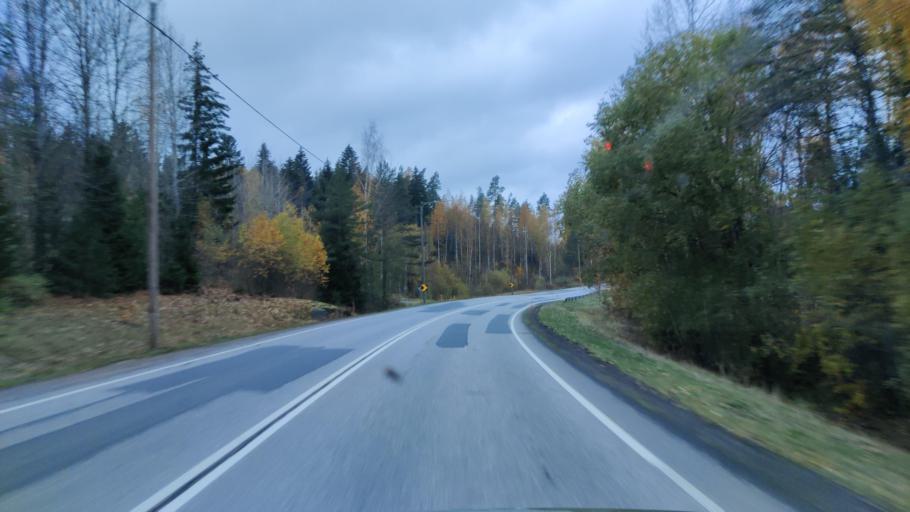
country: FI
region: Uusimaa
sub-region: Helsinki
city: Vihti
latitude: 60.3349
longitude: 24.2018
